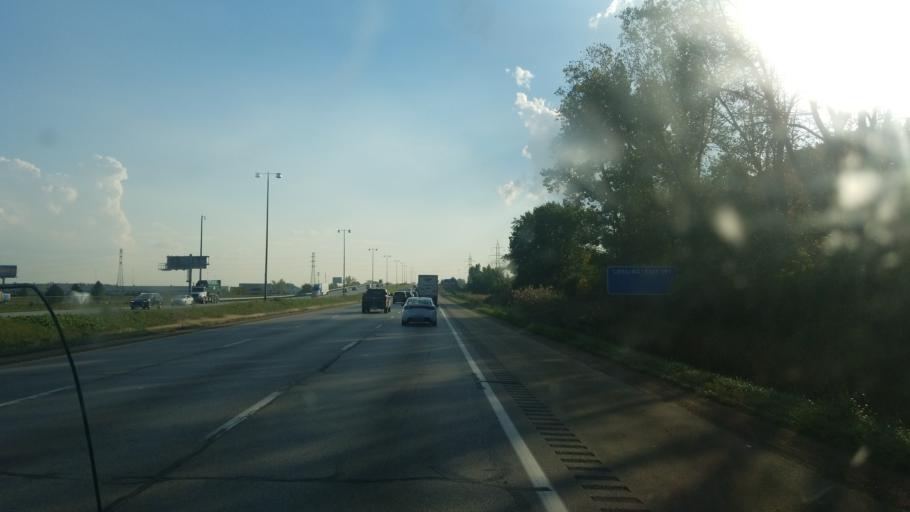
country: US
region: Ohio
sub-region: Wood County
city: Rossford
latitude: 41.5986
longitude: -83.5513
